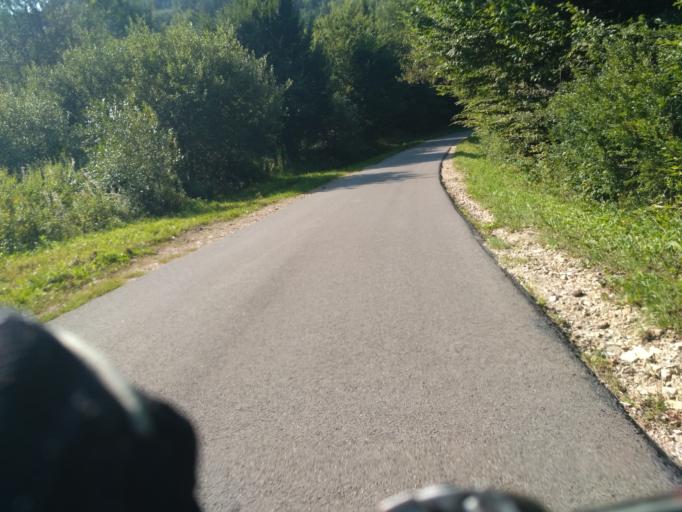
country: PL
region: Subcarpathian Voivodeship
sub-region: Powiat brzozowski
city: Golcowa
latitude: 49.7896
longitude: 22.0241
